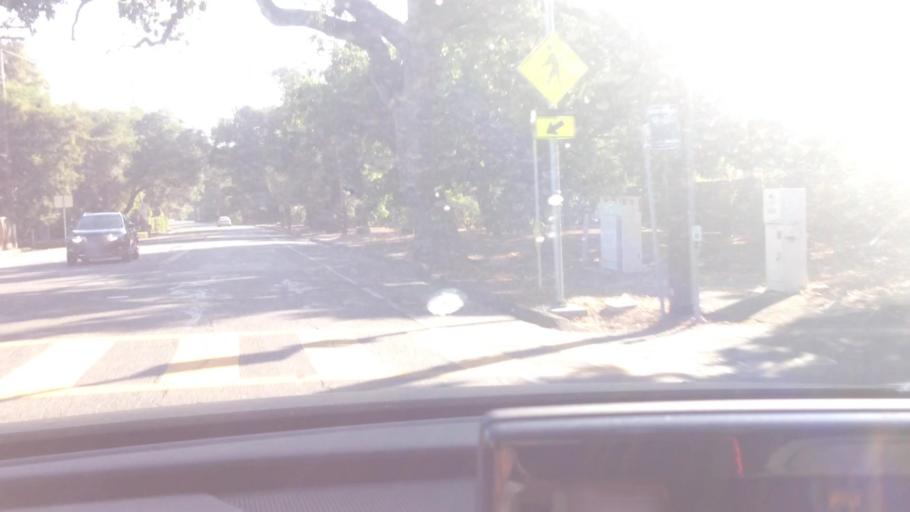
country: US
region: California
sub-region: Santa Clara County
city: Saratoga
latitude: 37.2652
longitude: -122.0220
